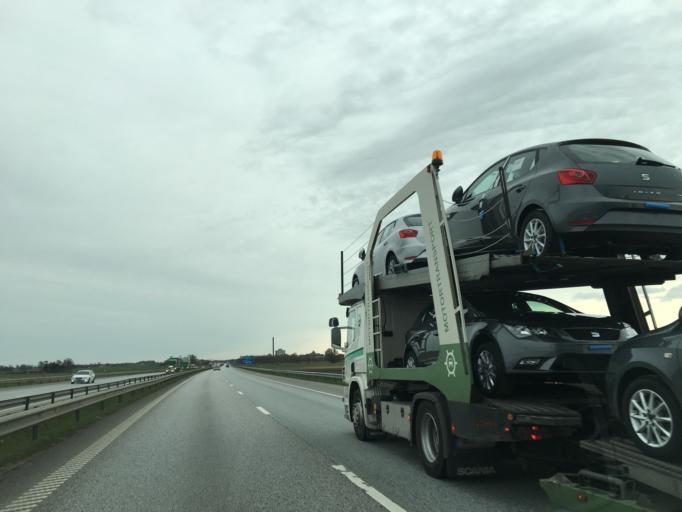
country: SE
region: Skane
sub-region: Lomma Kommun
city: Lomma
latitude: 55.7019
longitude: 13.0976
